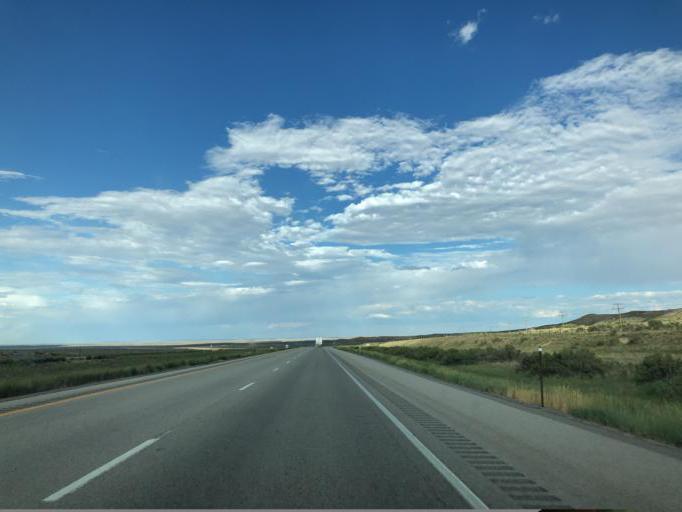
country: US
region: Wyoming
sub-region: Sweetwater County
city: Rock Springs
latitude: 41.6393
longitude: -108.2186
